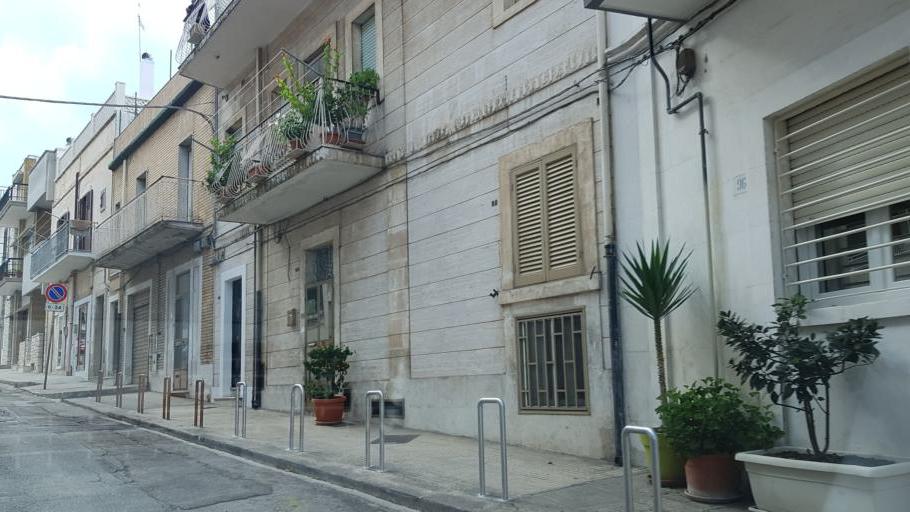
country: IT
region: Apulia
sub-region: Provincia di Brindisi
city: Ostuni
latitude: 40.7292
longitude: 17.5741
